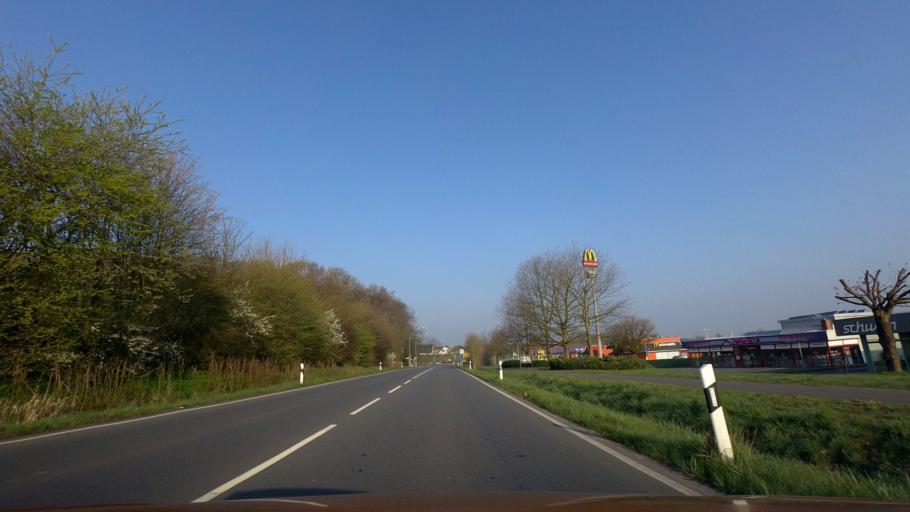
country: DE
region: Lower Saxony
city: Melle
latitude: 52.1896
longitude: 8.3548
